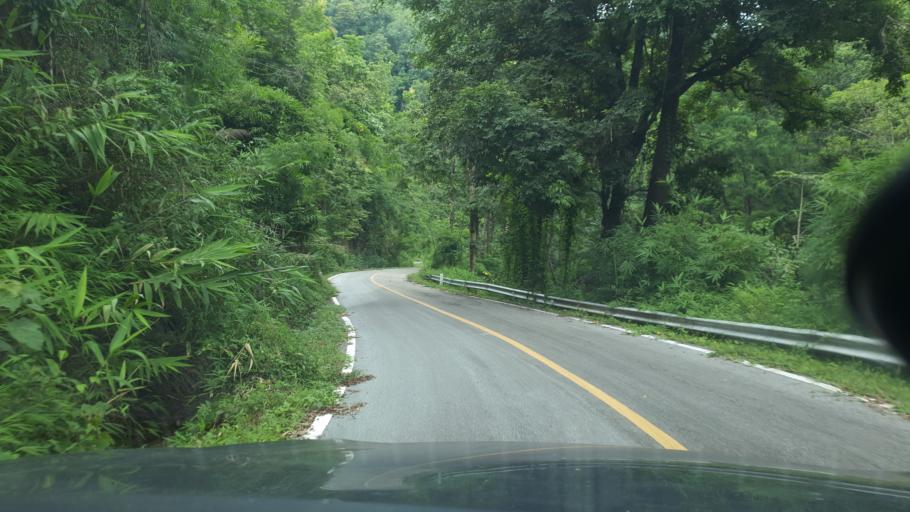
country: TH
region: Lamphun
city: Mae Tha
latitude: 18.4874
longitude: 99.2679
